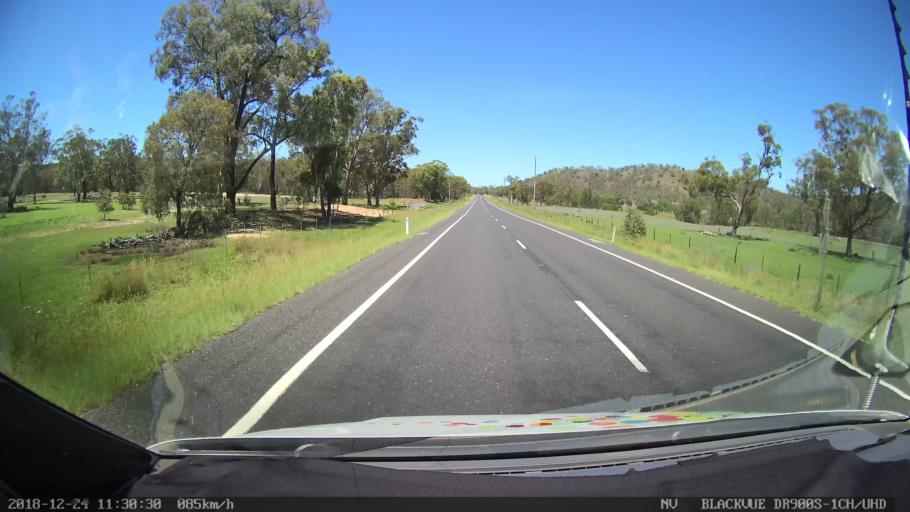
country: AU
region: New South Wales
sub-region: Upper Hunter Shire
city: Merriwa
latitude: -32.2053
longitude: 150.4659
